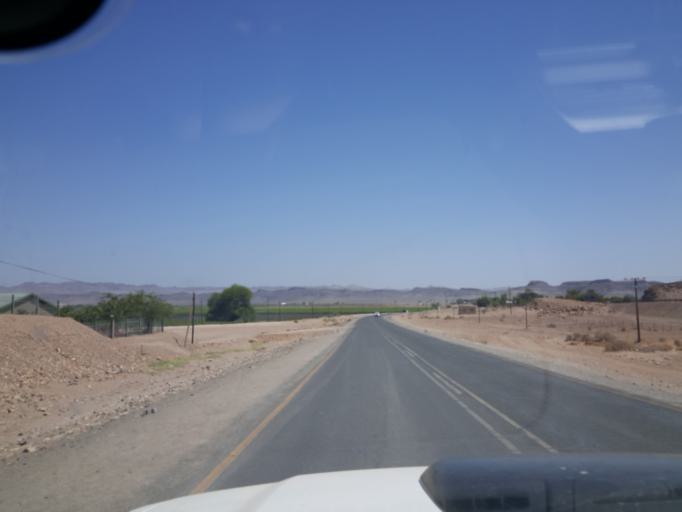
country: ZA
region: Northern Cape
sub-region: Namakwa District Municipality
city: Port Nolloth
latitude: -28.7339
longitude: 17.6160
